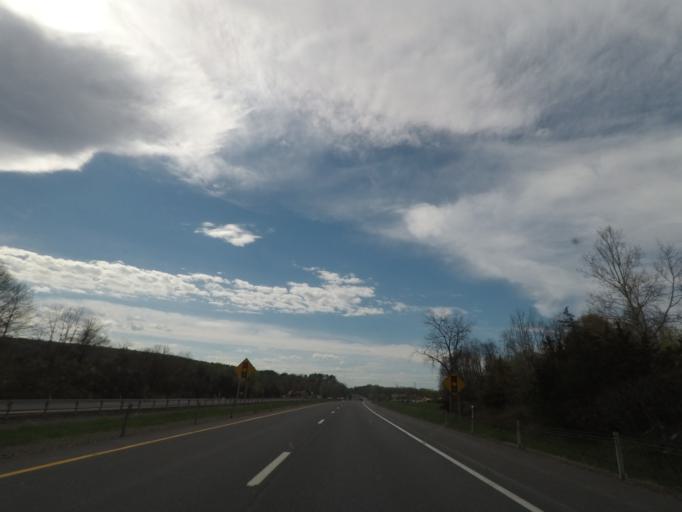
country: US
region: New York
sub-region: Greene County
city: Jefferson Heights
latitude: 42.2508
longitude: -73.9033
